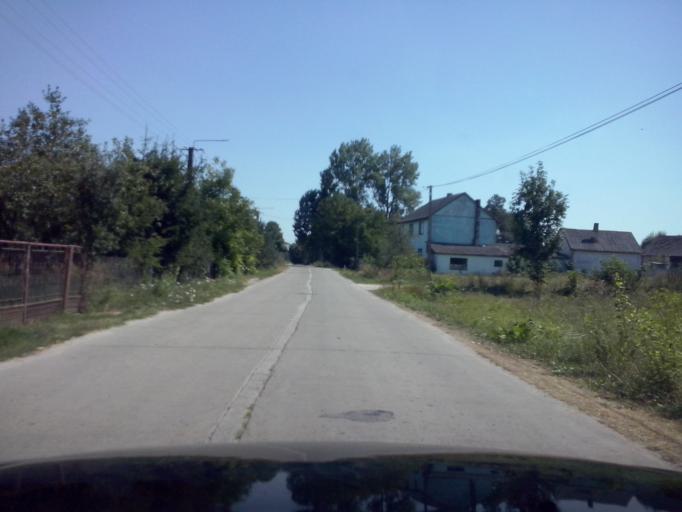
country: PL
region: Swietokrzyskie
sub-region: Powiat buski
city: Gnojno
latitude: 50.5992
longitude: 20.8054
